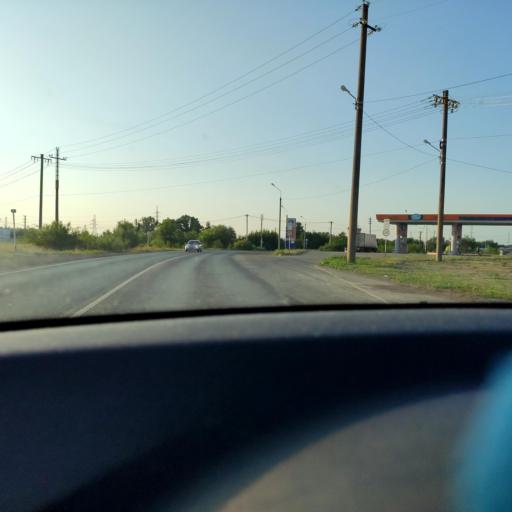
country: RU
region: Samara
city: Kinel'
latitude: 53.2377
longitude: 50.5805
